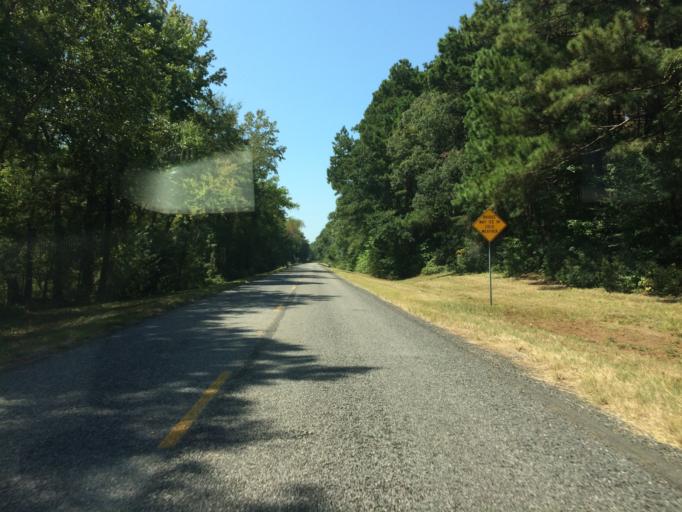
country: US
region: Texas
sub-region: Wood County
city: Hawkins
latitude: 32.7329
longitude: -95.2274
